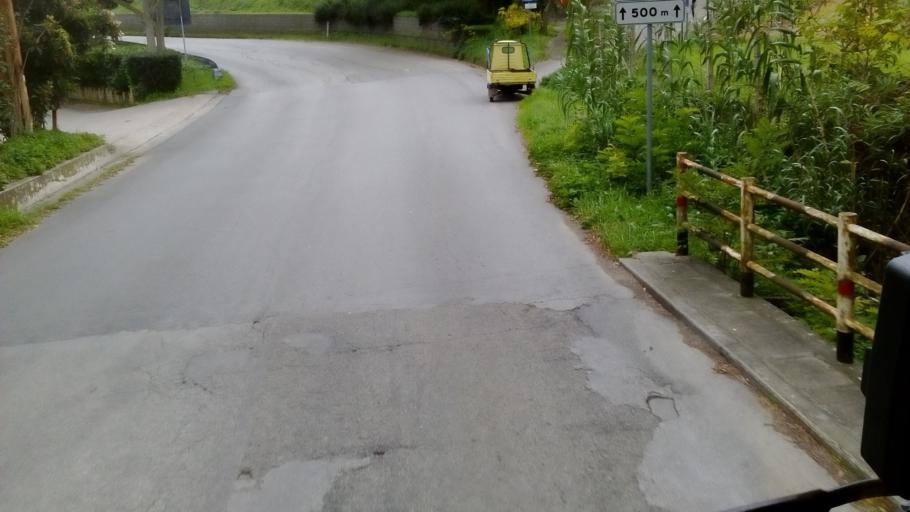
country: IT
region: Abruzzo
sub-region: Provincia di Chieti
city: San Salvo
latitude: 42.0573
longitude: 14.7278
